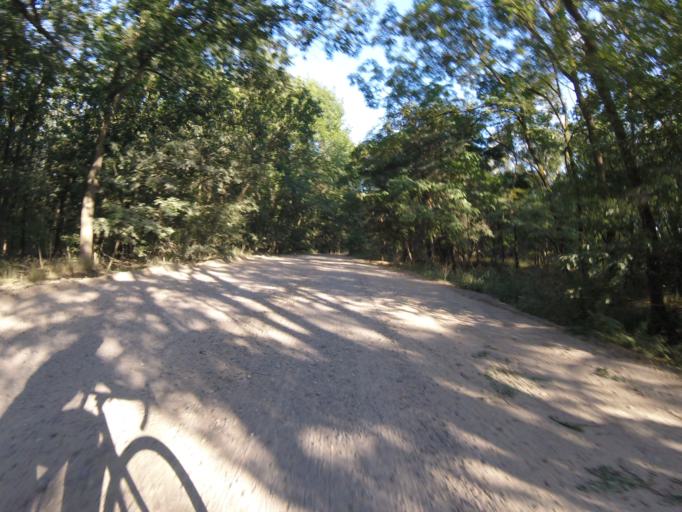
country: DE
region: Brandenburg
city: Zossen
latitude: 52.2007
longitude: 13.5009
